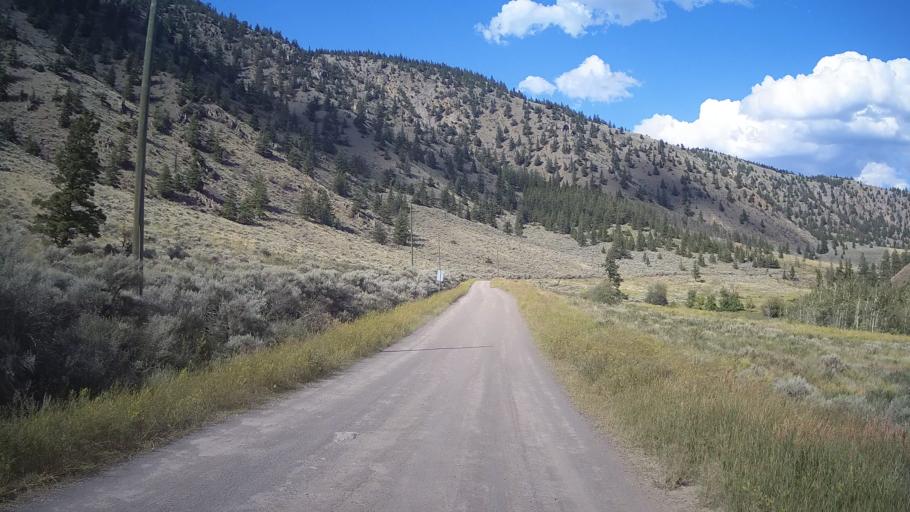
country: CA
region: British Columbia
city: Lillooet
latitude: 51.2165
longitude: -122.0943
